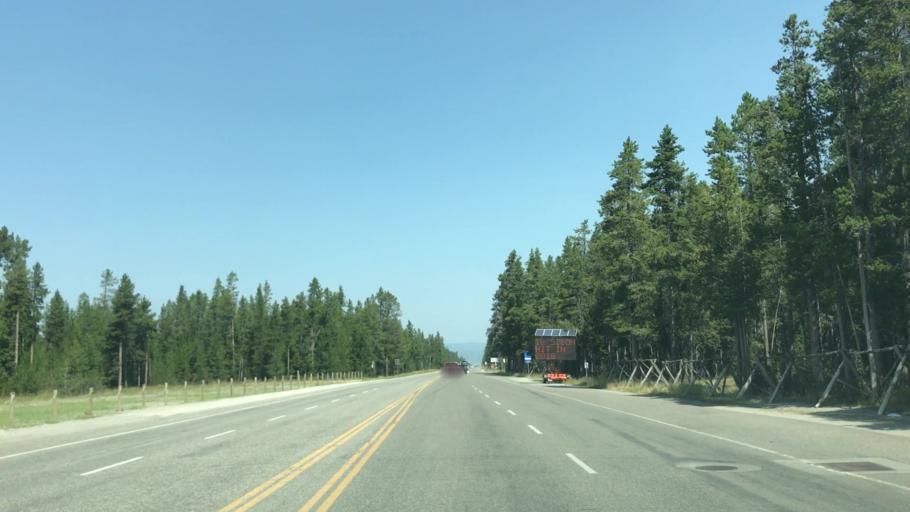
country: US
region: Montana
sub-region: Gallatin County
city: West Yellowstone
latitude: 44.6649
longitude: -111.0997
